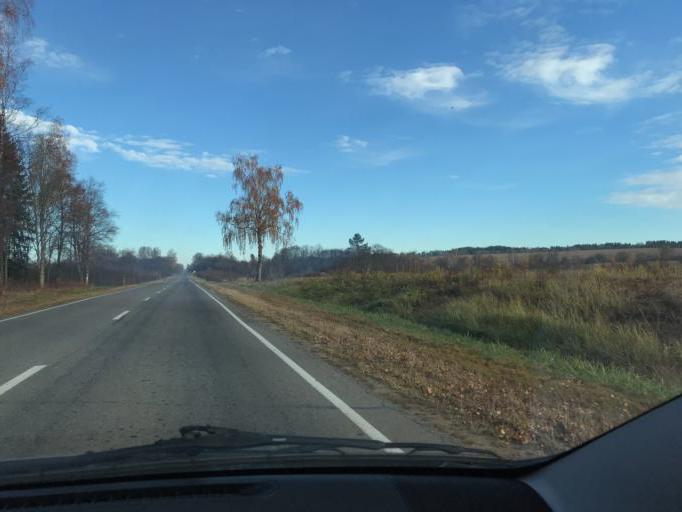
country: BY
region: Vitebsk
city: Haradok
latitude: 55.5189
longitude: 29.9710
